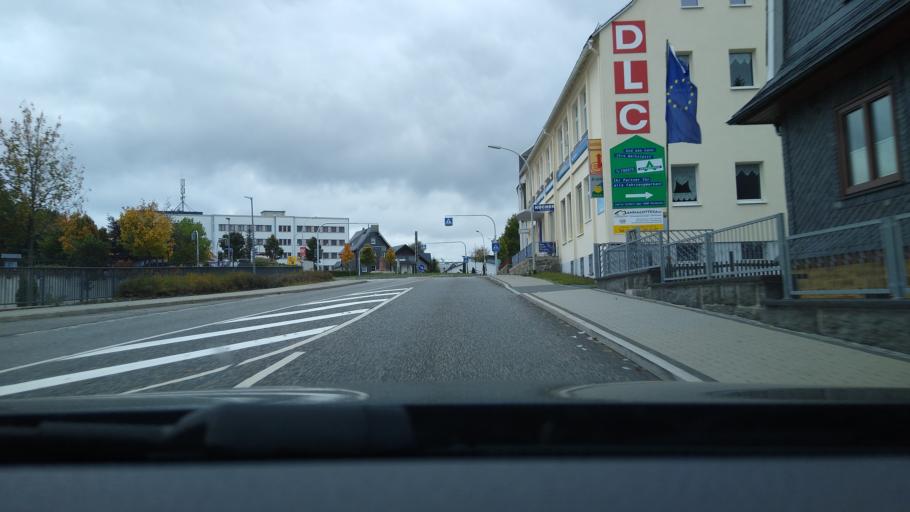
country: DE
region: Thuringia
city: Neuhaus am Rennweg
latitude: 50.5079
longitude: 11.1343
